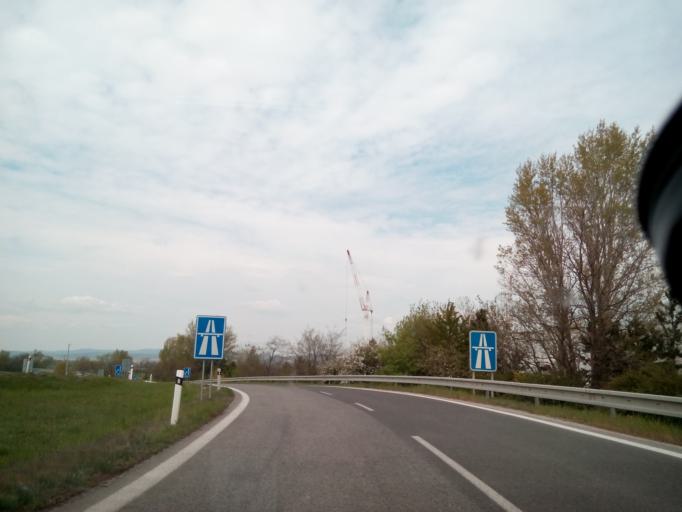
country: SK
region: Trnavsky
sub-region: Okres Trnava
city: Piestany
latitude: 48.5912
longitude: 17.7937
